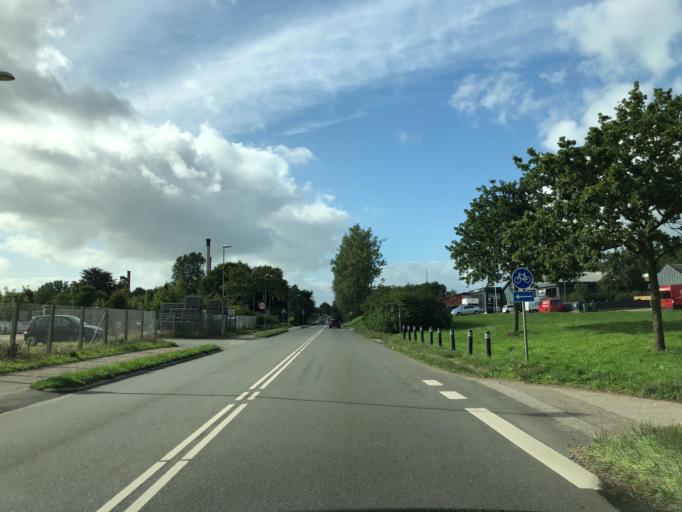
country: DK
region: Central Jutland
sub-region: Holstebro Kommune
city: Holstebro
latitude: 56.3650
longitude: 8.5889
